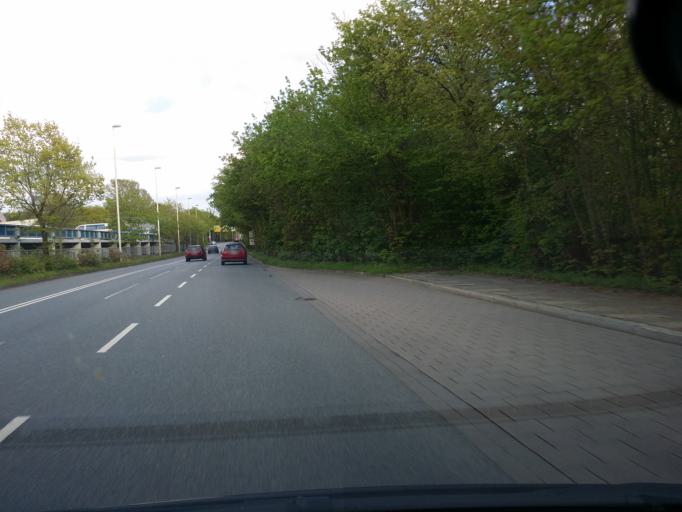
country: DE
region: Schleswig-Holstein
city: Rendsburg
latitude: 54.3043
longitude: 9.6606
